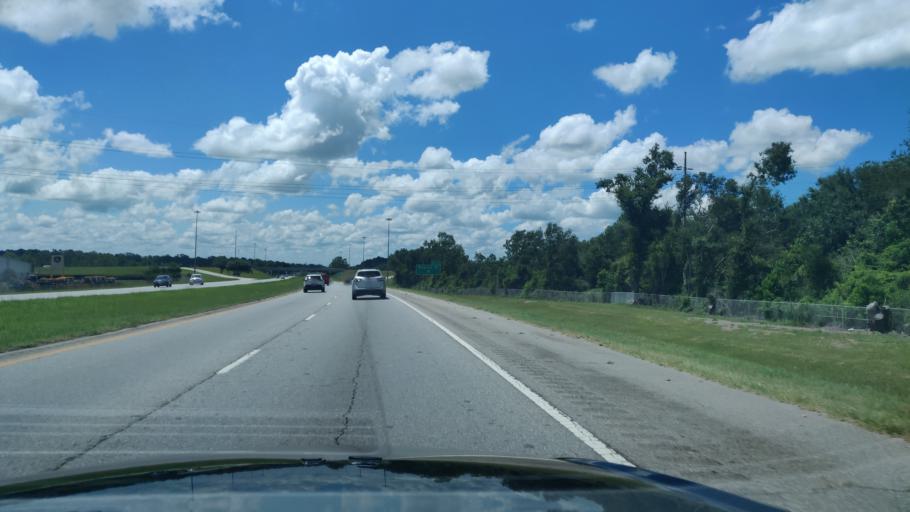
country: US
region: Georgia
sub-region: Dougherty County
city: Albany
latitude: 31.5904
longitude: -84.1193
